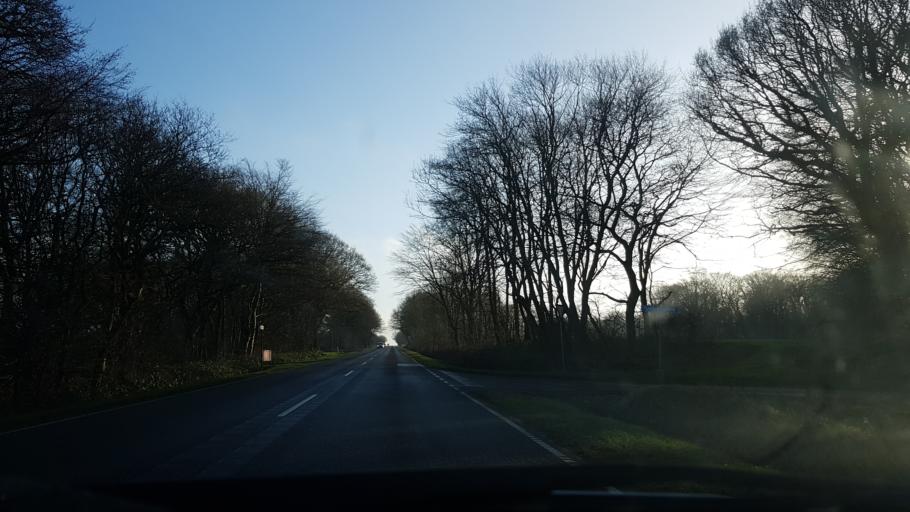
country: DK
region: South Denmark
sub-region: Tonder Kommune
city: Toftlund
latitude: 55.2226
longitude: 9.1772
